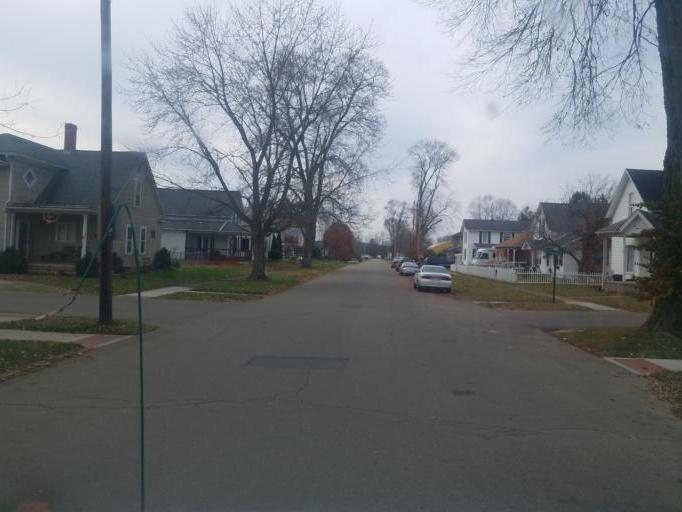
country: US
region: Ohio
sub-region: Knox County
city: Mount Vernon
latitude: 40.3924
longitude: -82.4999
